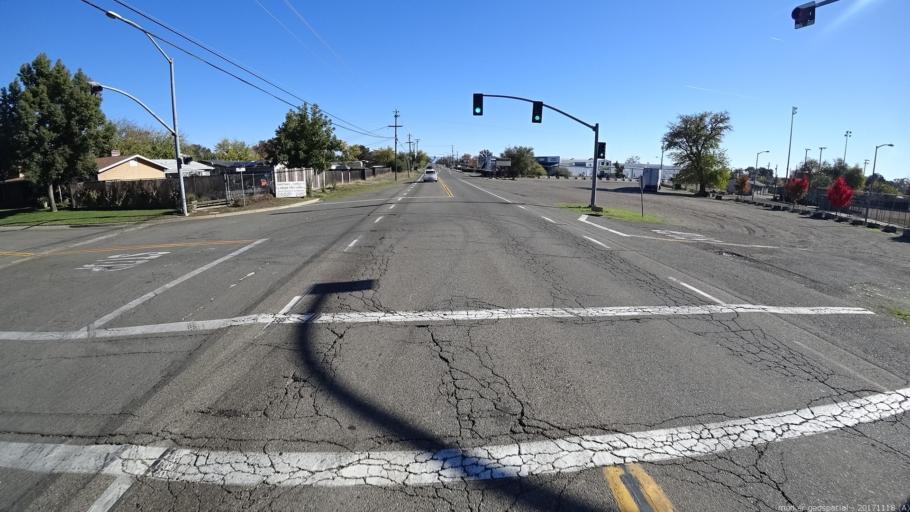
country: US
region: California
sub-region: Shasta County
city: Cottonwood
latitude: 40.3893
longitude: -122.2903
